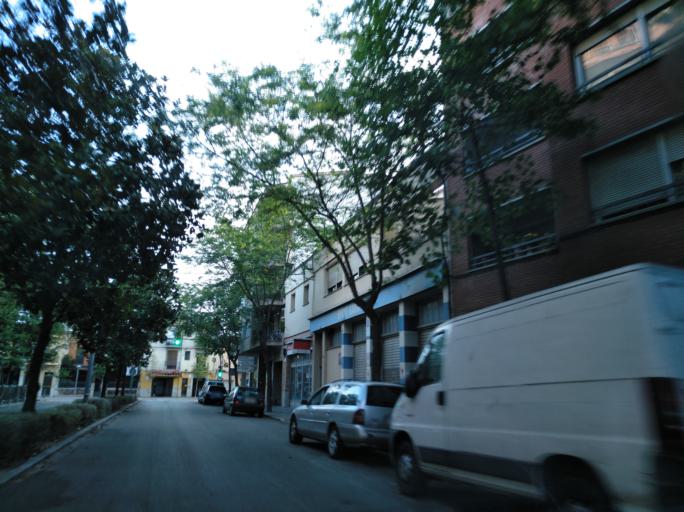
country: ES
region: Catalonia
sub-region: Provincia de Girona
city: Salt
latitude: 41.9732
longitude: 2.7860
